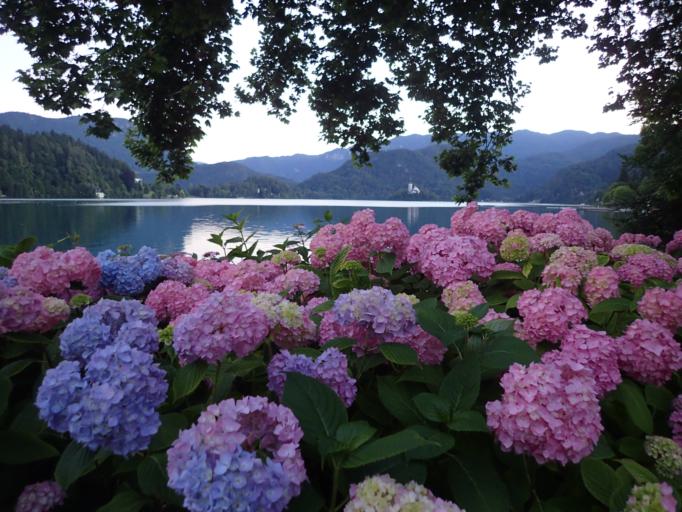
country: SI
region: Bled
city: Bled
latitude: 46.3711
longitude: 14.0997
